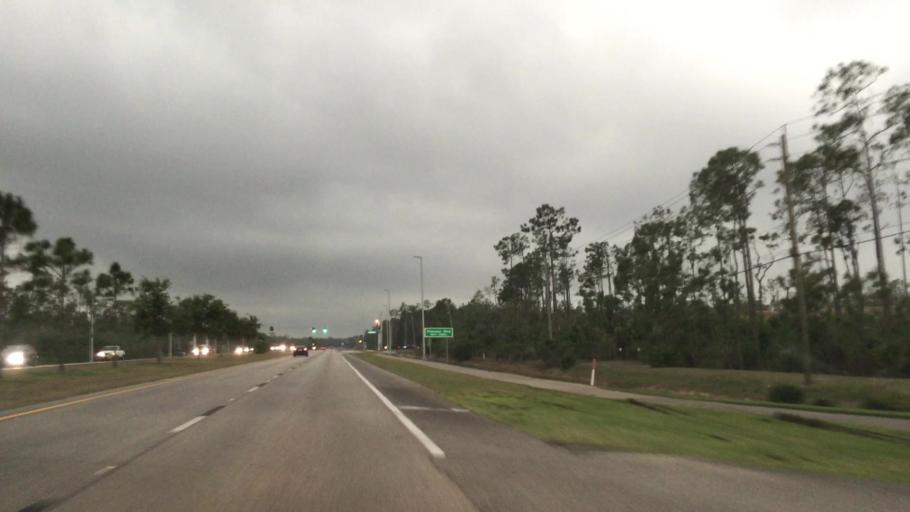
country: US
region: Florida
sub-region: Lee County
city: Villas
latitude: 26.5731
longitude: -81.8270
